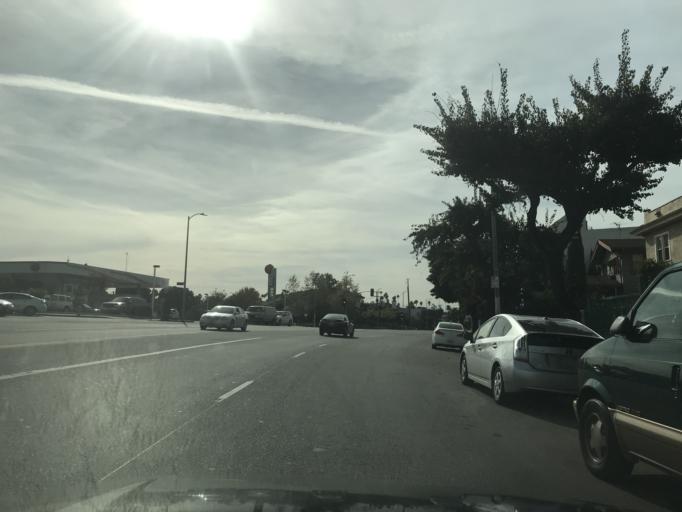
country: US
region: California
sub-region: Los Angeles County
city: Hollywood
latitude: 34.0536
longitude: -118.3144
